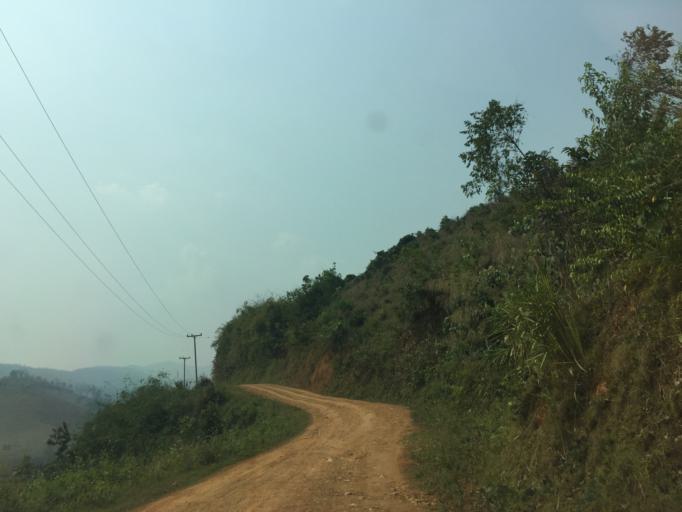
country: TH
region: Phayao
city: Phu Sang
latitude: 19.5794
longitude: 100.5275
